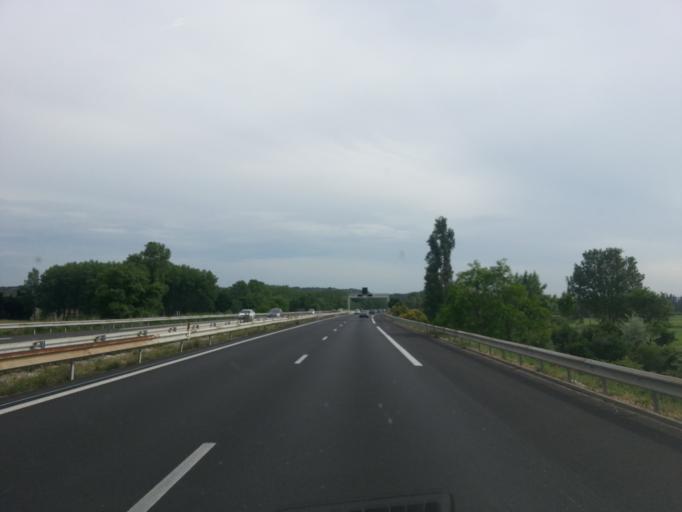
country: FR
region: Provence-Alpes-Cote d'Azur
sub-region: Departement du Vaucluse
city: Caderousse
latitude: 44.0998
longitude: 4.7887
